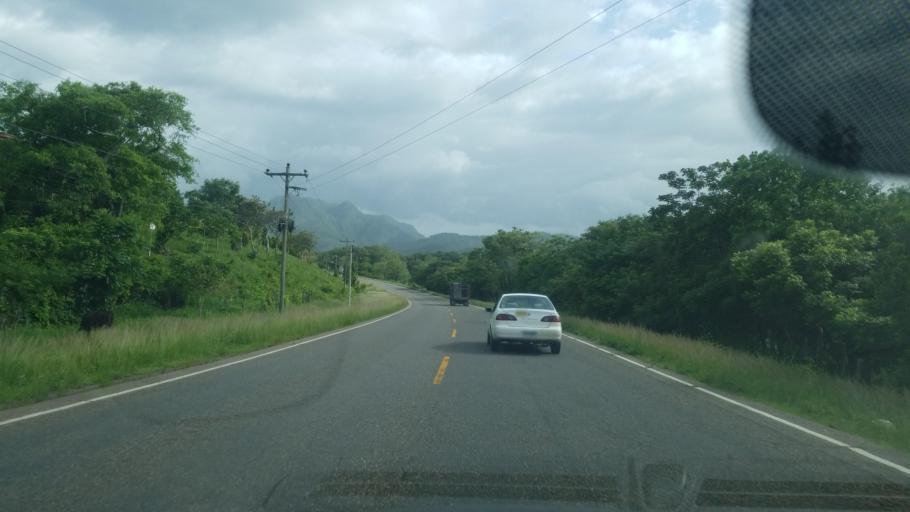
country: HN
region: Ocotepeque
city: Antigua Ocotepeque
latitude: 14.3872
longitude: -89.2063
